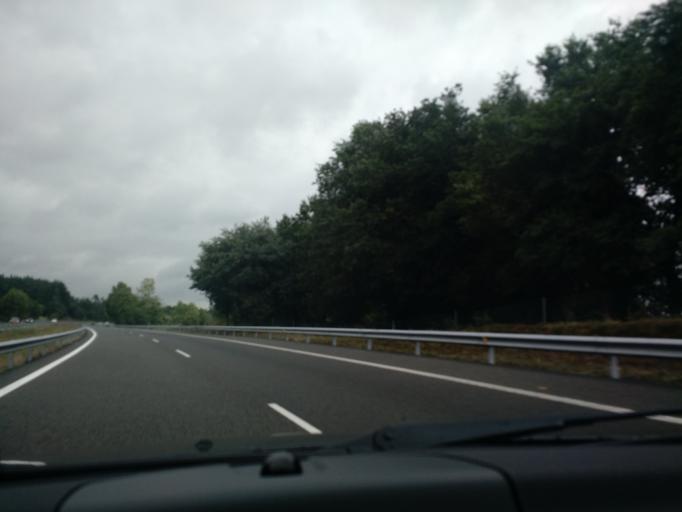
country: ES
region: Galicia
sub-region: Provincia da Coruna
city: Oroso
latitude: 43.0057
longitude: -8.4193
